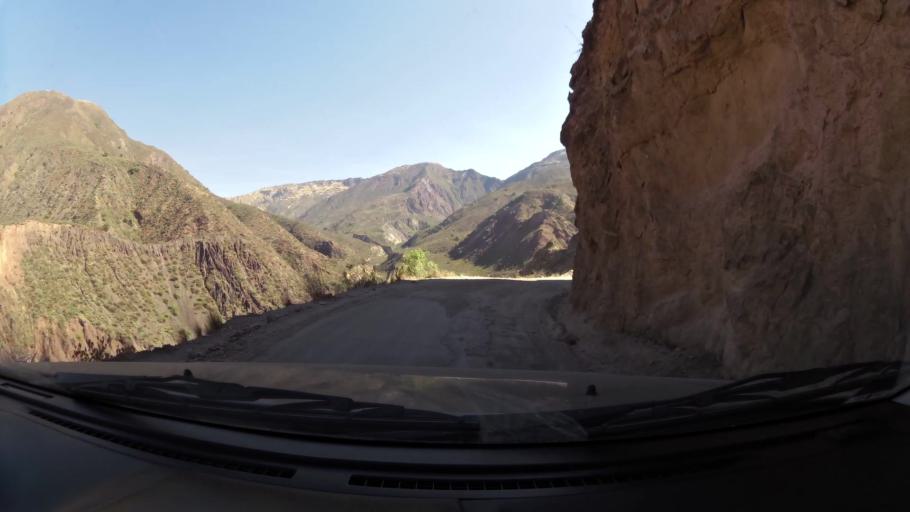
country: PE
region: Huancavelica
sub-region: Provincia de Acobamba
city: Pomacocha
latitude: -12.7856
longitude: -74.4931
